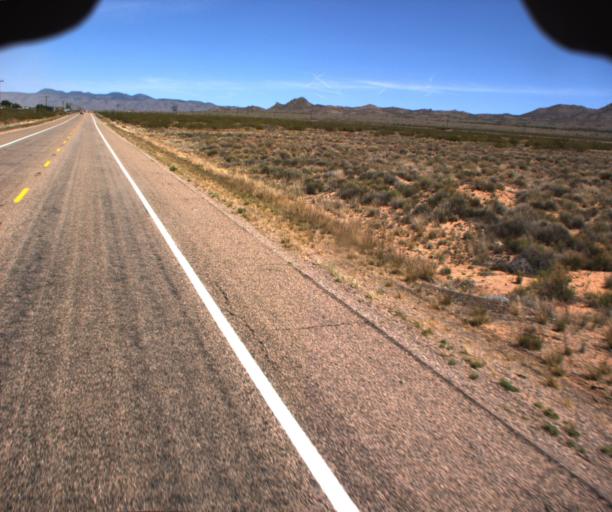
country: US
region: Arizona
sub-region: Mohave County
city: New Kingman-Butler
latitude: 35.3771
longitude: -113.8576
